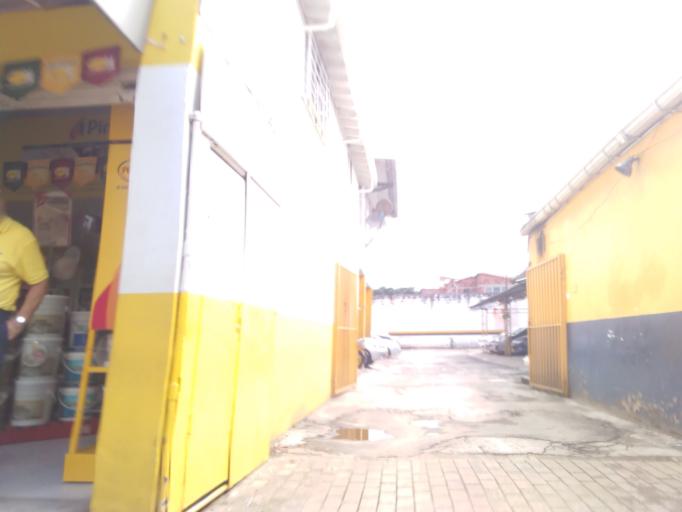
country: CO
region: Antioquia
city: Medellin
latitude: 6.2343
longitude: -75.5962
